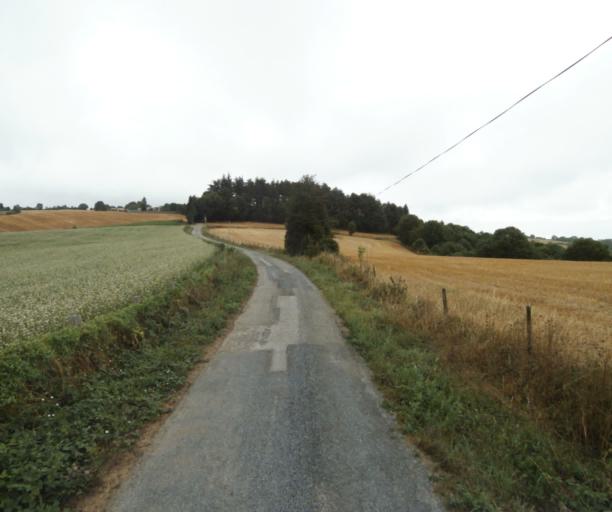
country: FR
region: Midi-Pyrenees
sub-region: Departement du Tarn
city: Soreze
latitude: 43.4006
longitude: 2.0425
